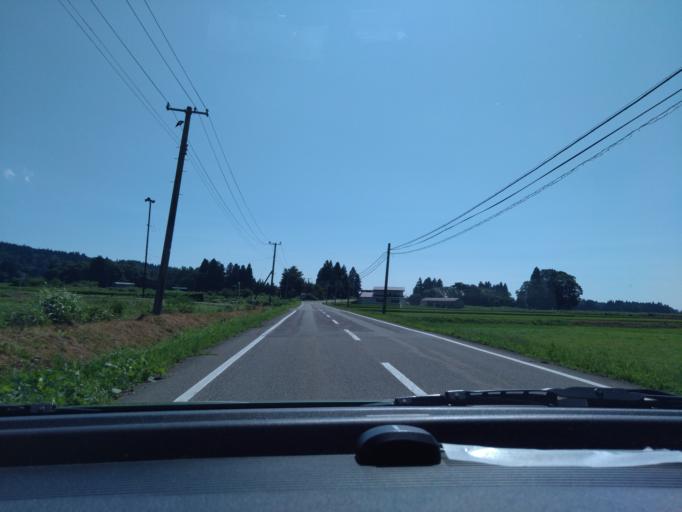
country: JP
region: Akita
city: Kakunodatemachi
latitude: 39.4844
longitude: 140.6233
